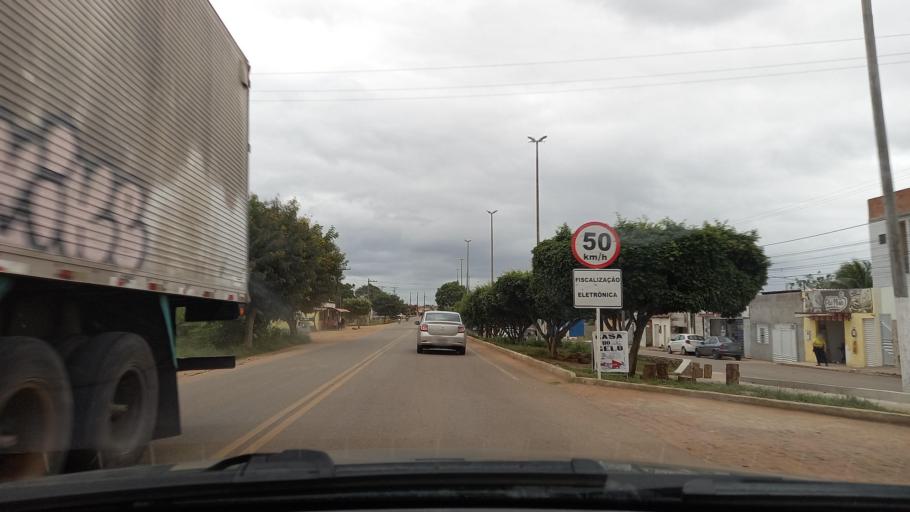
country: BR
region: Sergipe
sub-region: Caninde De Sao Francisco
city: Caninde de Sao Francisco
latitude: -9.6762
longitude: -37.7925
